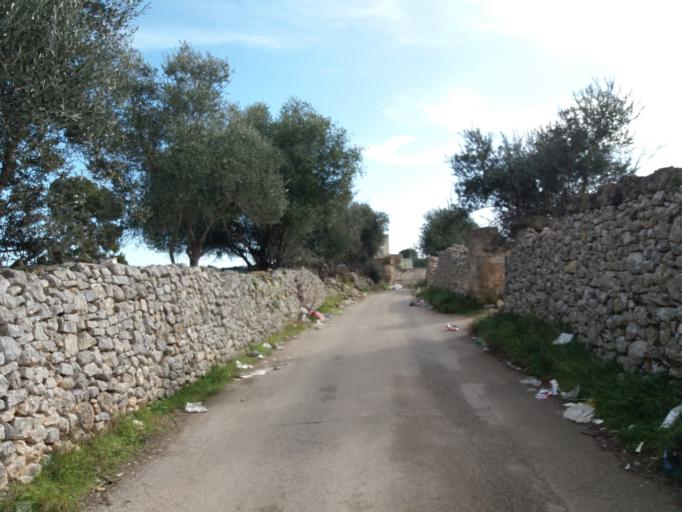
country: IT
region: Apulia
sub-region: Provincia di Barletta - Andria - Trani
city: Andria
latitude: 41.2151
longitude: 16.3076
